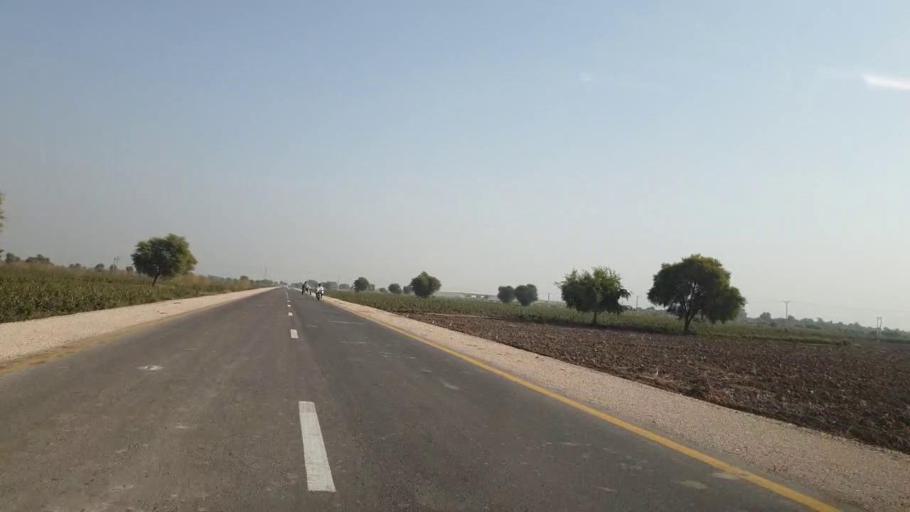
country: PK
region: Sindh
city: Sehwan
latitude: 26.4656
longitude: 67.7976
